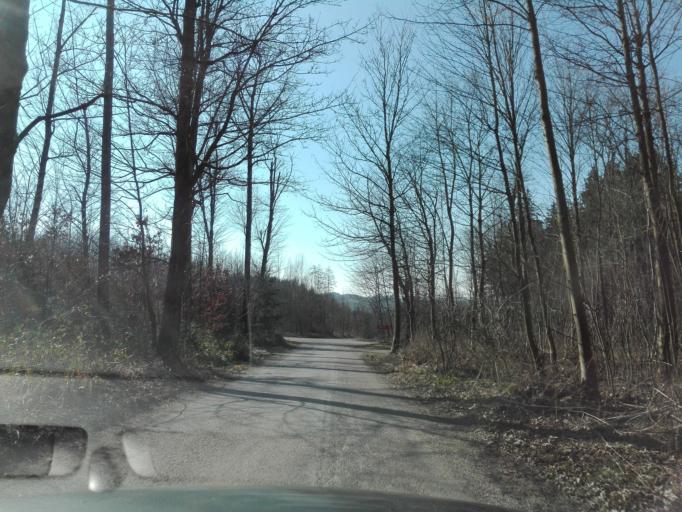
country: AT
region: Upper Austria
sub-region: Wels-Land
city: Buchkirchen
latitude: 48.2489
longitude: 14.0597
